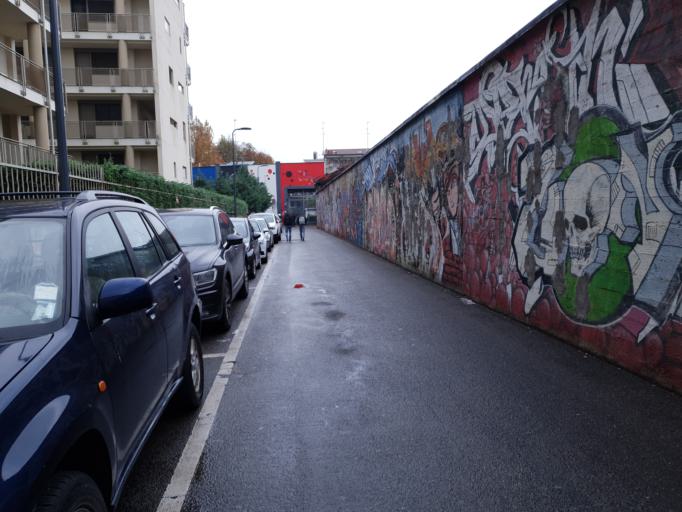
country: IT
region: Lombardy
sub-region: Citta metropolitana di Milano
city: Cormano
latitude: 45.5071
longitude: 9.1677
